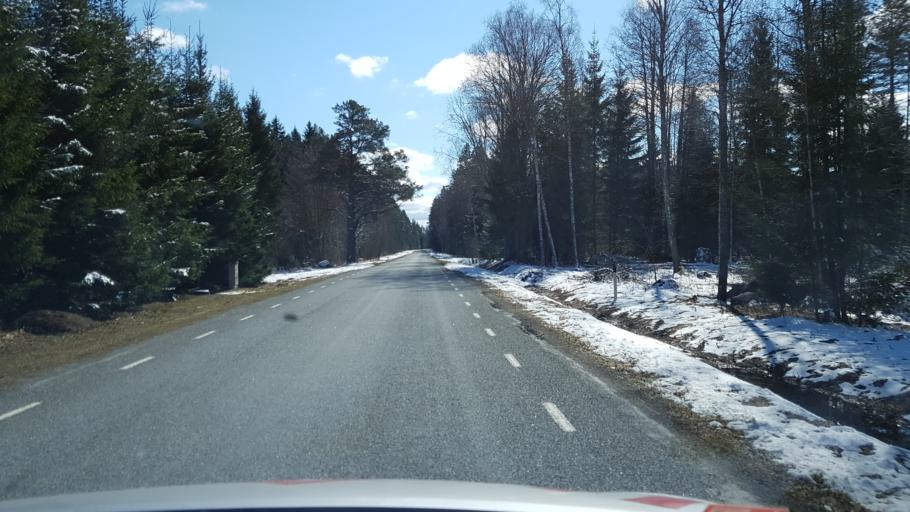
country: EE
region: Laeaene-Virumaa
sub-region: Kadrina vald
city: Kadrina
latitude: 59.4912
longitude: 25.9844
